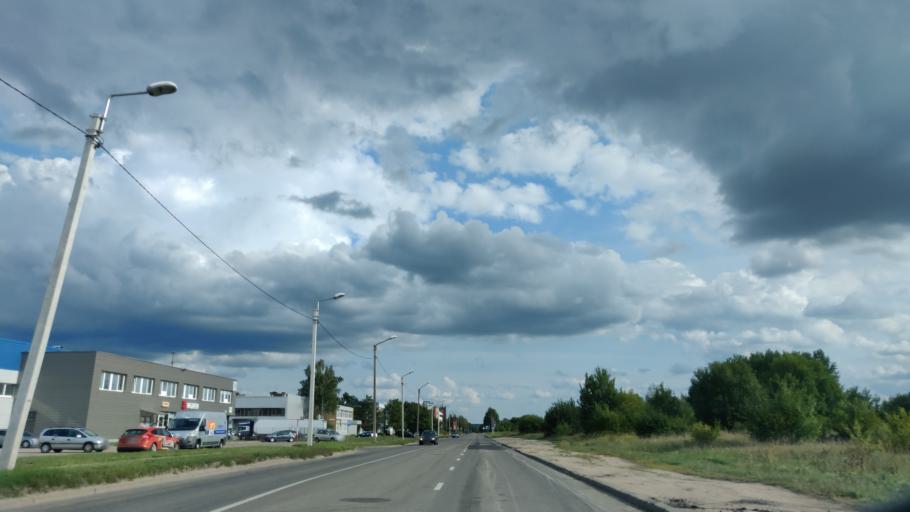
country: LT
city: Baltoji Voke
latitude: 54.6286
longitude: 25.1377
